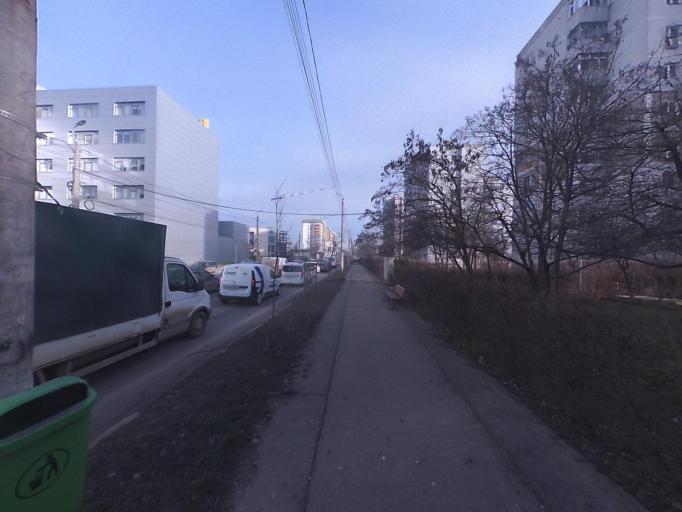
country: RO
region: Iasi
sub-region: Municipiul Iasi
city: Iasi
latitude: 47.1366
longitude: 27.5980
